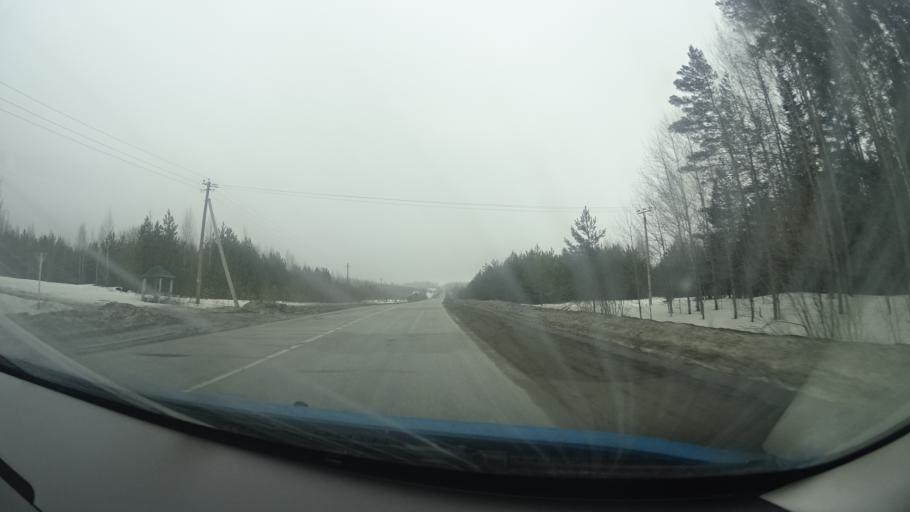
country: RU
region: Perm
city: Kuyeda
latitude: 56.4766
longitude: 55.7643
